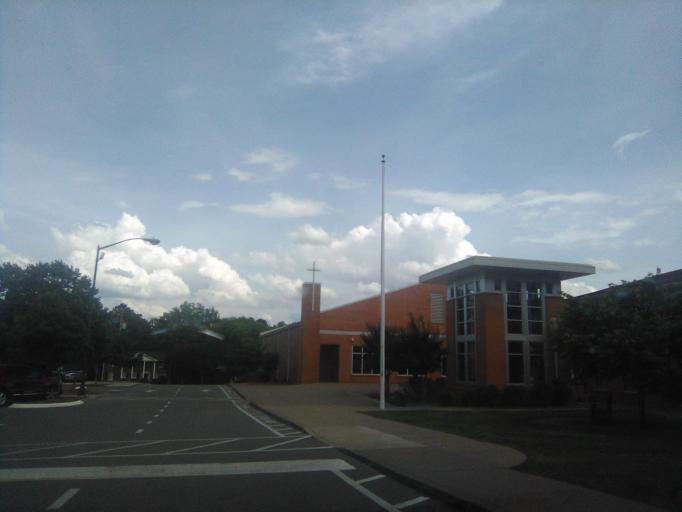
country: US
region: Tennessee
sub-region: Davidson County
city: Belle Meade
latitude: 36.0907
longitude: -86.8865
